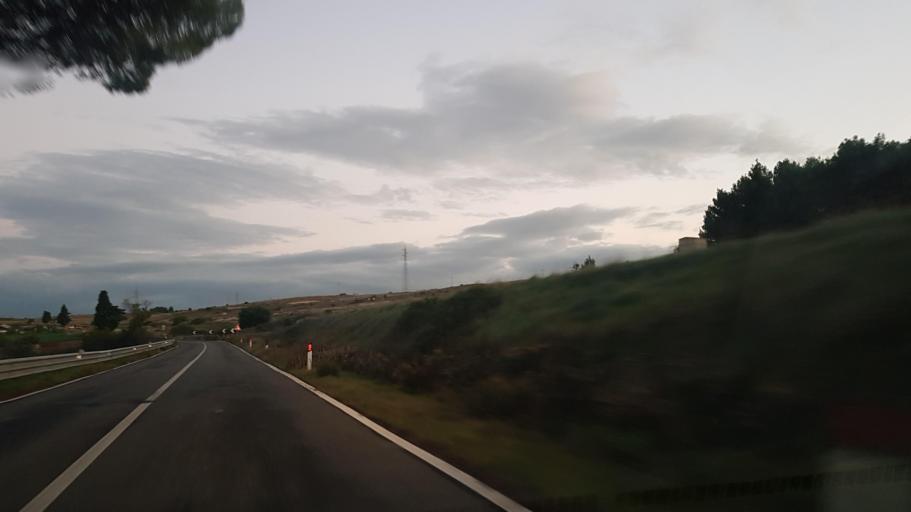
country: IT
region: Basilicate
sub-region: Provincia di Matera
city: Matera
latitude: 40.6771
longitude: 16.6774
